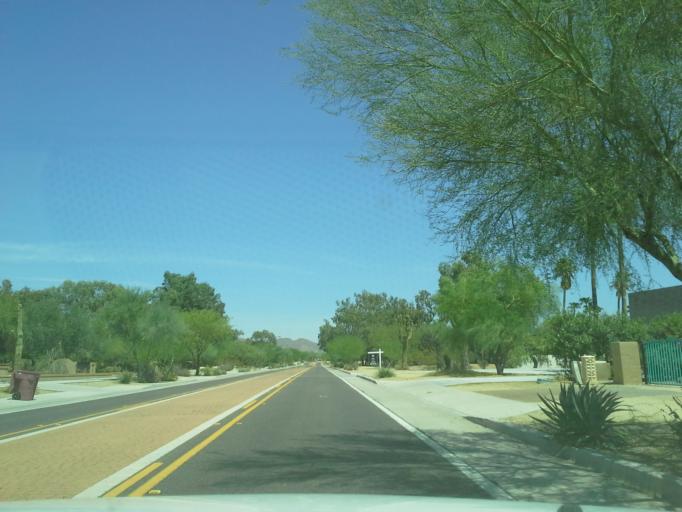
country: US
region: Arizona
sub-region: Maricopa County
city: Scottsdale
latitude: 33.5970
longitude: -111.8619
